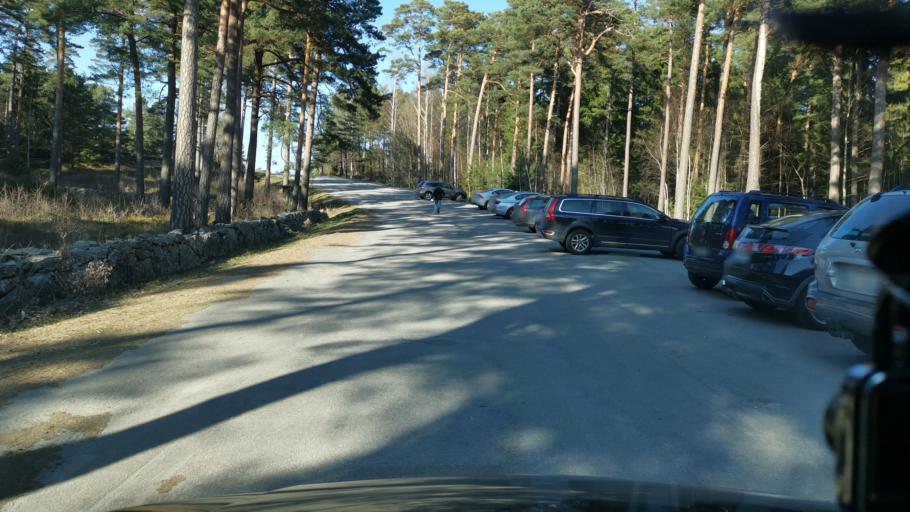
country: SE
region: Vaestra Goetaland
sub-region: Stenungsunds Kommun
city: Stenungsund
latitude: 58.0602
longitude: 11.7996
